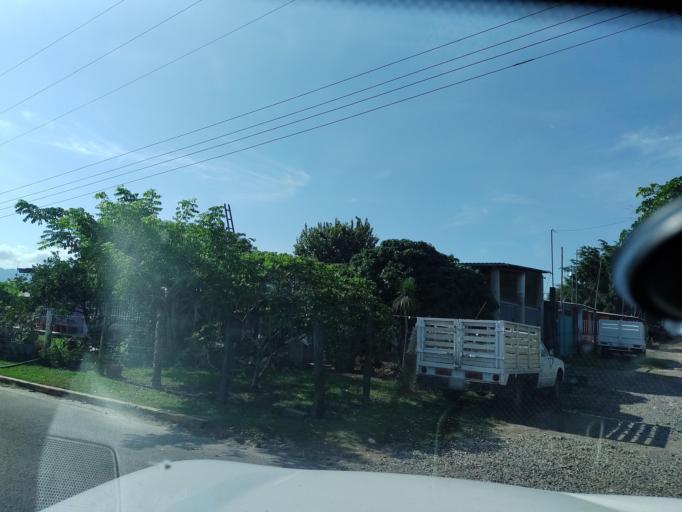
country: MX
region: Veracruz
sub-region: Martinez de la Torre
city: El Progreso
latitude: 20.1120
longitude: -96.9887
